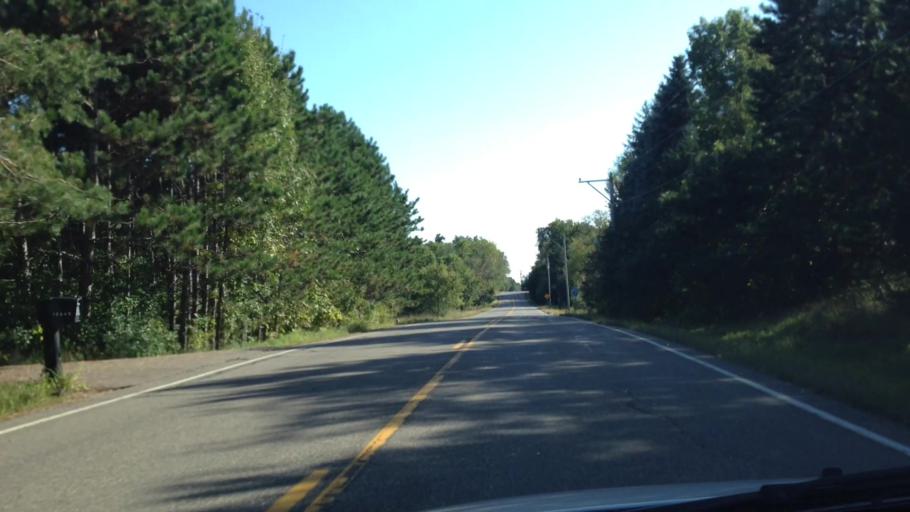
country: US
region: Minnesota
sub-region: Washington County
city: Stillwater
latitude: 45.1033
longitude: -92.8129
